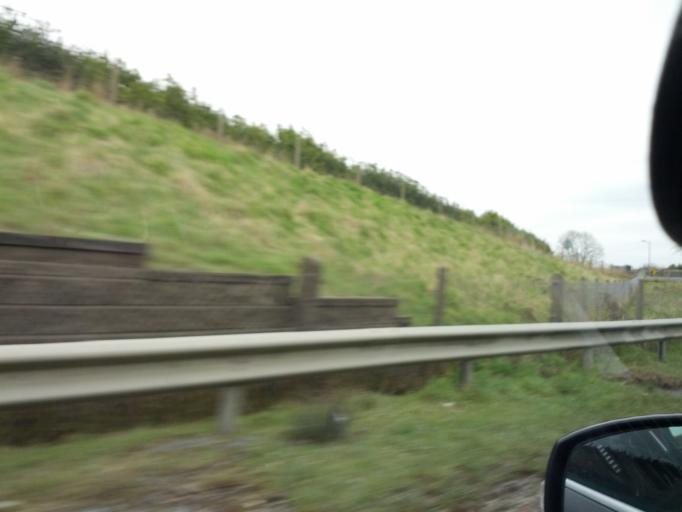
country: IE
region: Connaught
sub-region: County Galway
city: Athenry
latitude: 53.2463
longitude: -8.7482
